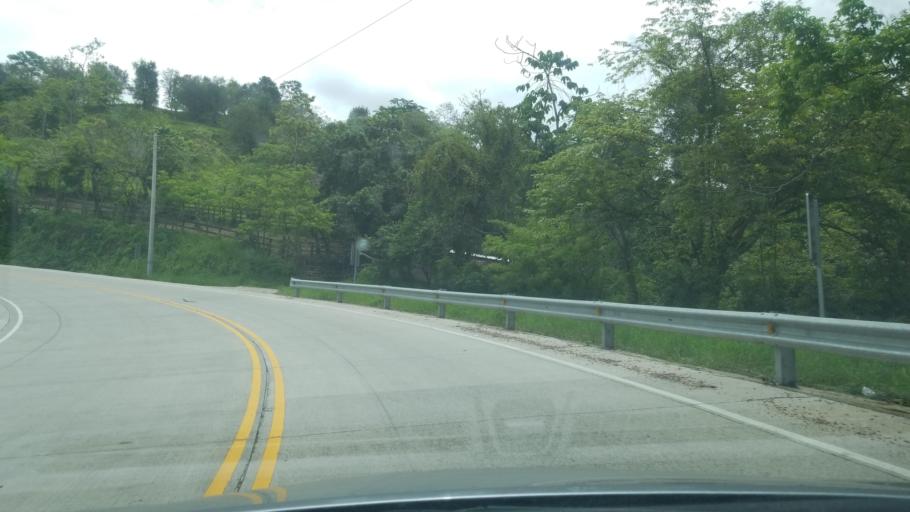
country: HN
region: Copan
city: Florida
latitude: 14.9990
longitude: -88.8427
